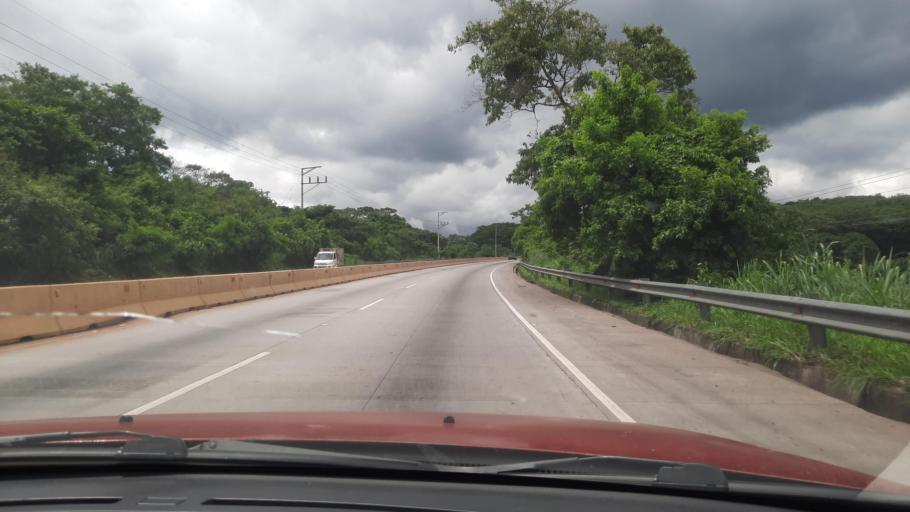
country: SV
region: Sonsonate
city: Sonzacate
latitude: 13.7335
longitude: -89.7003
